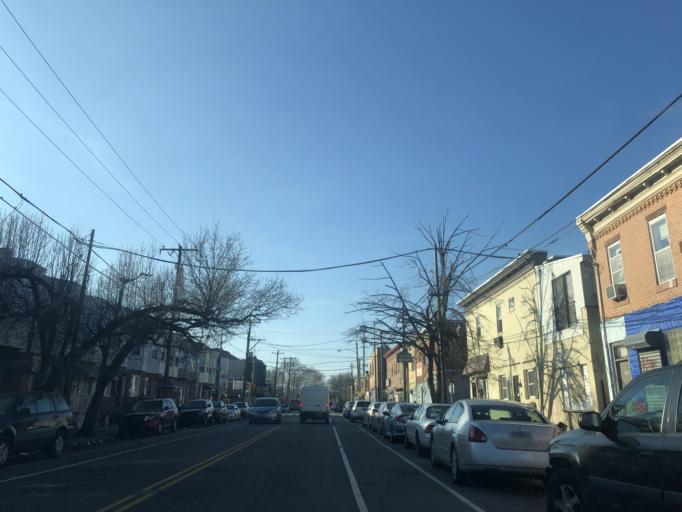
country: US
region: Pennsylvania
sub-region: Philadelphia County
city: Philadelphia
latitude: 39.9262
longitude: -75.1833
